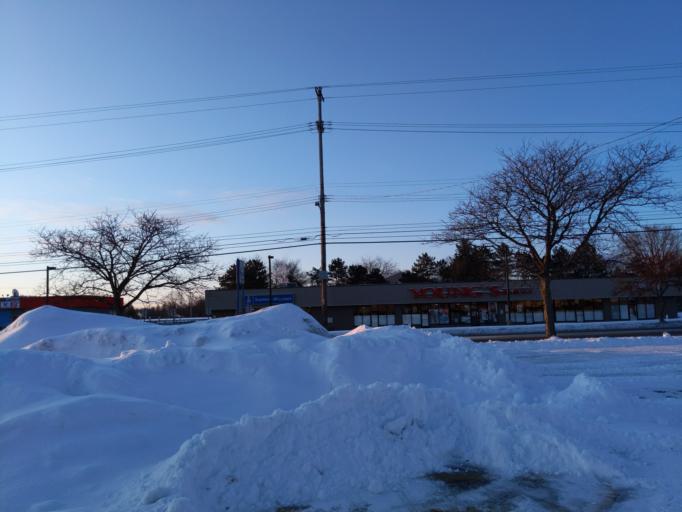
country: US
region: Michigan
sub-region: Ingham County
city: Lansing
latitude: 42.6978
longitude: -84.5704
